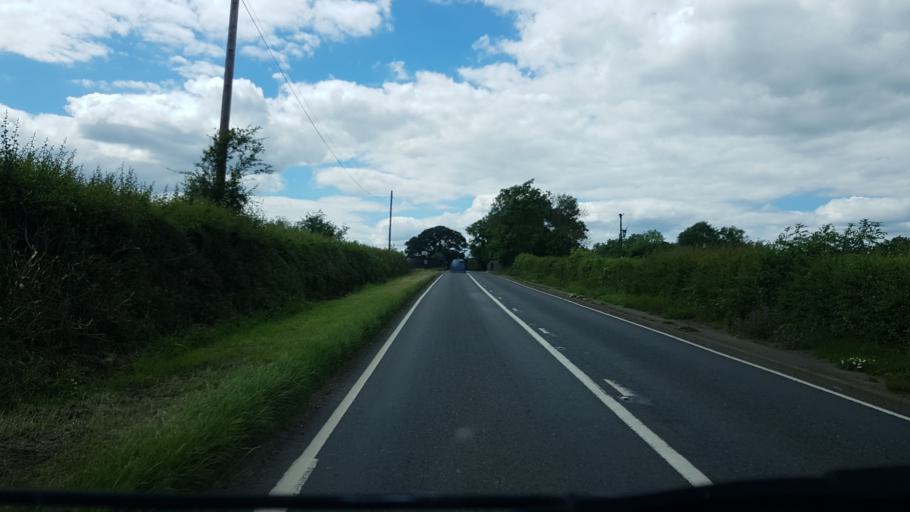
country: GB
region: England
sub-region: Worcestershire
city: Droitwich
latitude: 52.2634
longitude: -2.1060
